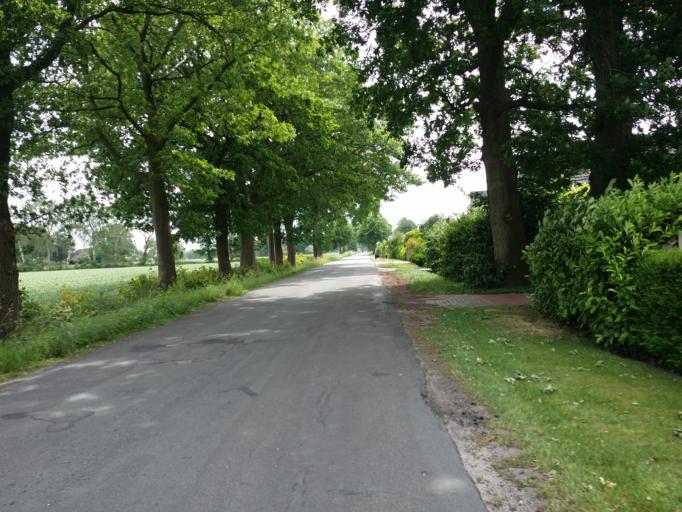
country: DE
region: Lower Saxony
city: Bockhorn
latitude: 53.3387
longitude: 8.0311
